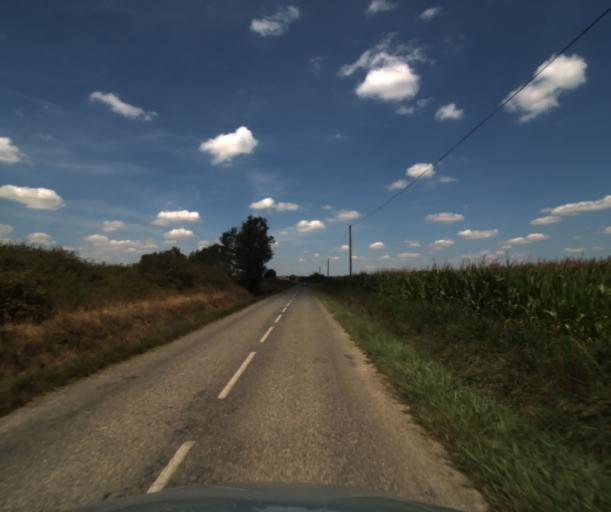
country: FR
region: Midi-Pyrenees
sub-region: Departement de la Haute-Garonne
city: Saint-Lys
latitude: 43.4963
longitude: 1.1784
